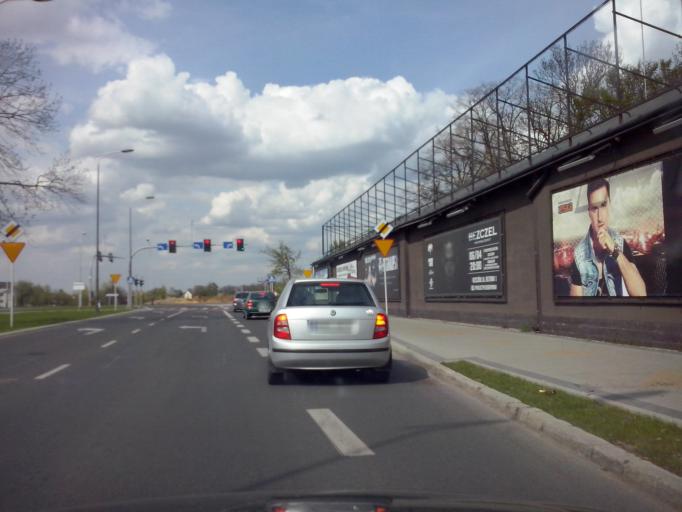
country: PL
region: Subcarpathian Voivodeship
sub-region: Rzeszow
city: Rzeszow
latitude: 50.0379
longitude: 22.0169
